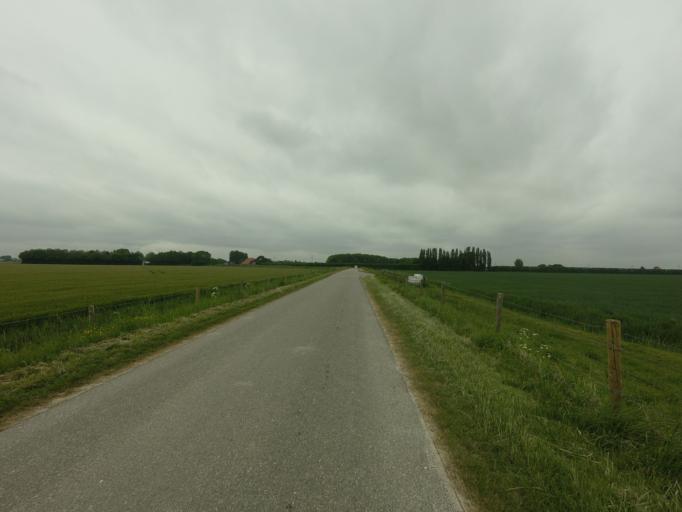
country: NL
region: South Holland
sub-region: Gemeente Spijkenisse
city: Spijkenisse
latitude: 51.7950
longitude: 4.3426
